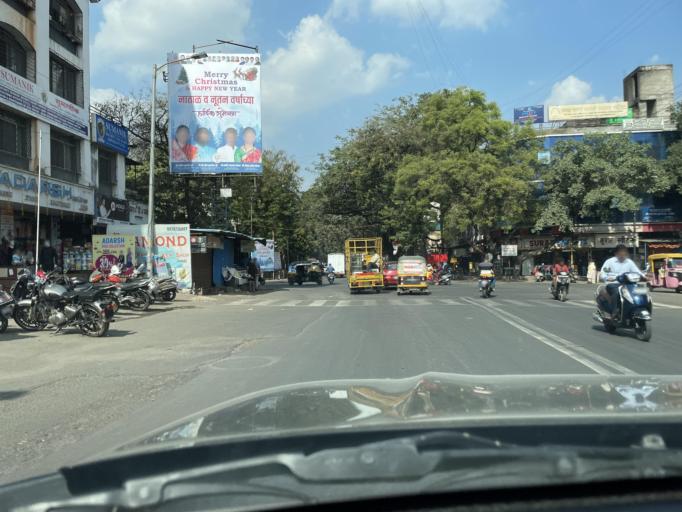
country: IN
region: Maharashtra
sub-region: Pune Division
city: Pune
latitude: 18.4947
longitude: 73.9000
